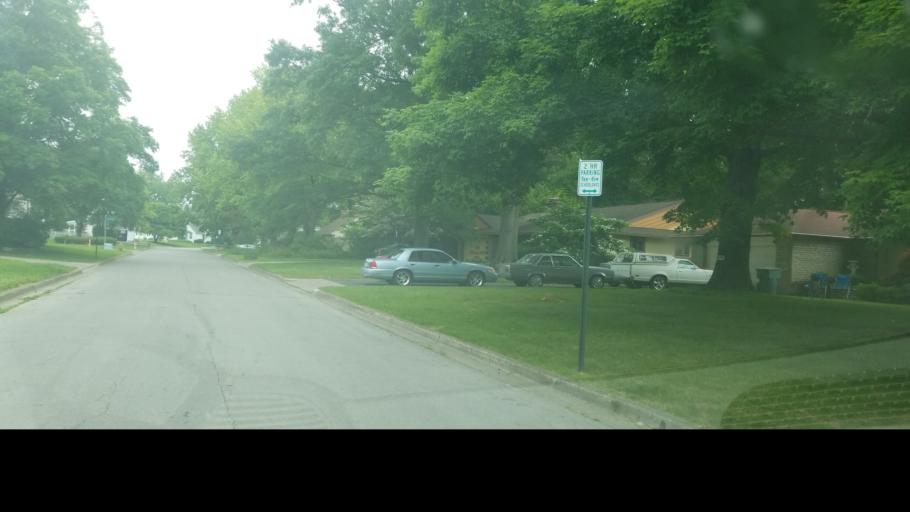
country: US
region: Ohio
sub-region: Franklin County
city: Worthington
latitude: 40.0505
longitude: -83.0118
